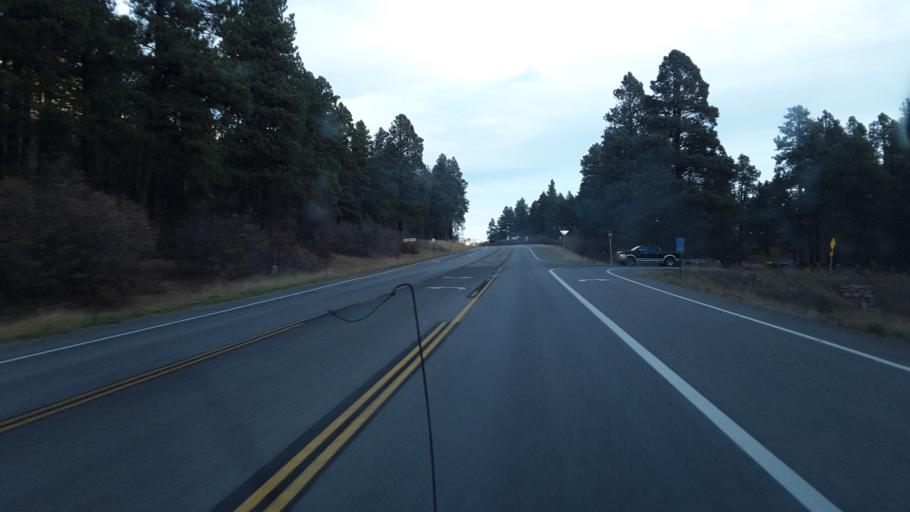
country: US
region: Colorado
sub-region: La Plata County
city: Durango
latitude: 37.4886
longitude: -107.8152
